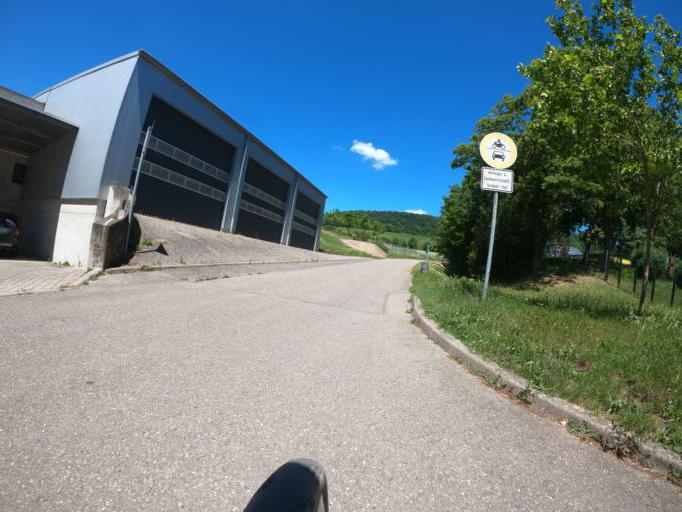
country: DE
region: Baden-Wuerttemberg
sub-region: Regierungsbezirk Stuttgart
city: Sersheim
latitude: 49.0015
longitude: 9.0207
